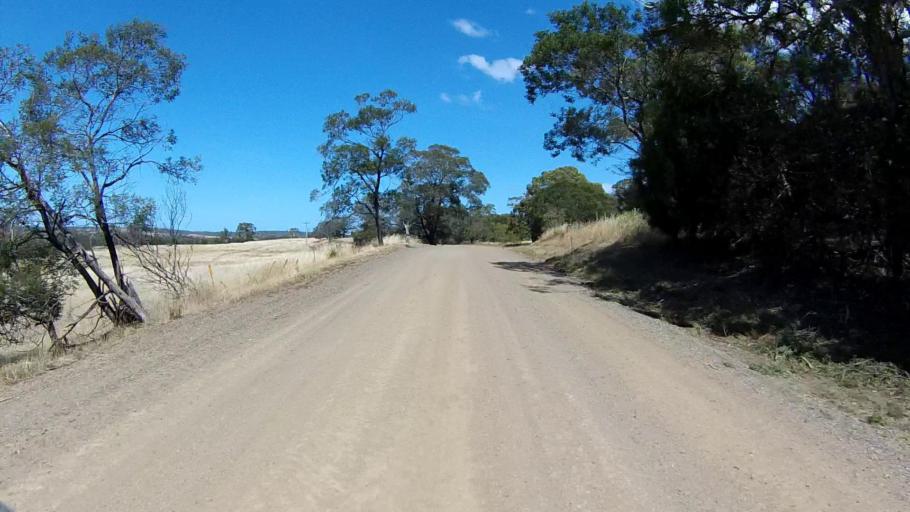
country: AU
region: Tasmania
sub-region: Break O'Day
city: St Helens
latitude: -41.9710
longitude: 148.0728
